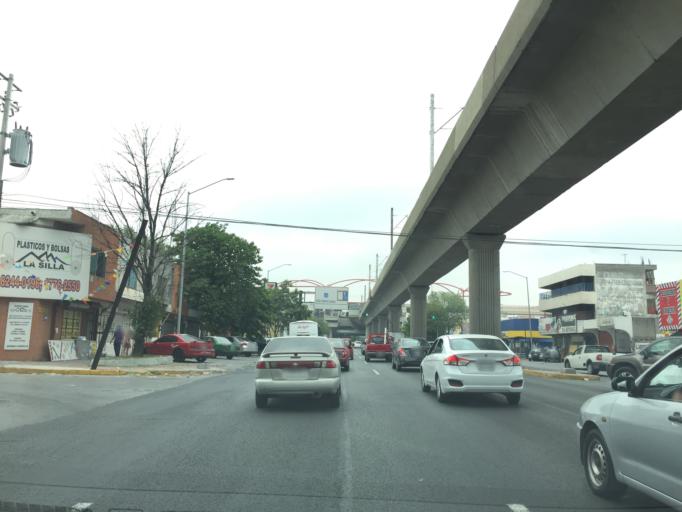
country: MX
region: Nuevo Leon
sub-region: Monterrey
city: Monterrey
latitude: 25.6838
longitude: -100.2942
